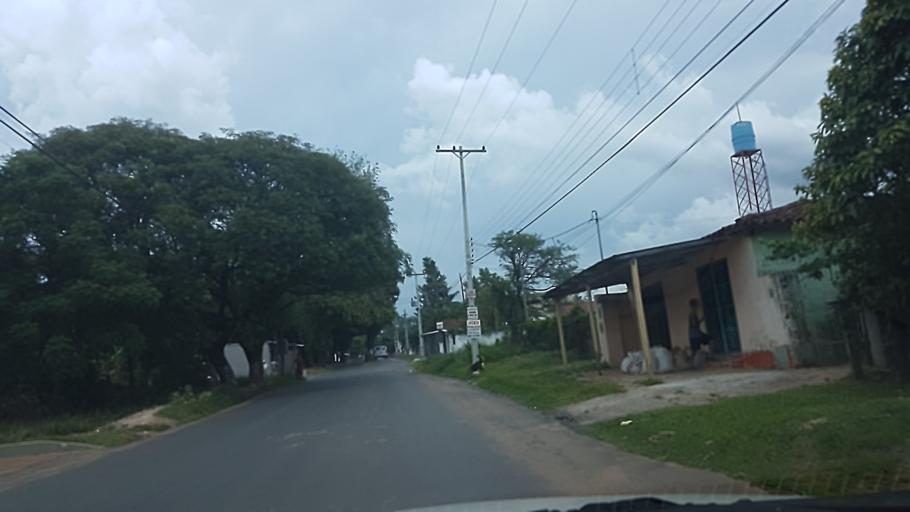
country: PY
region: Central
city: Colonia Mariano Roque Alonso
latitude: -25.2178
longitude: -57.5209
